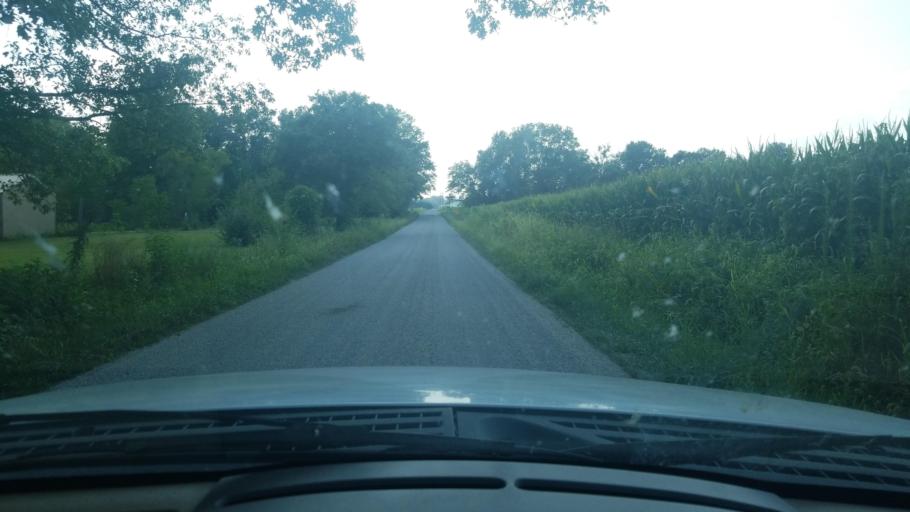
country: US
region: Illinois
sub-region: Saline County
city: Eldorado
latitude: 37.8345
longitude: -88.4391
